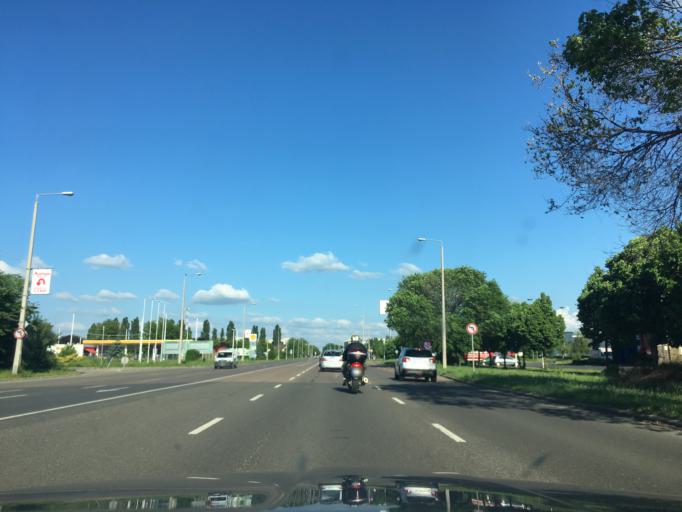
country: HU
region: Hajdu-Bihar
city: Debrecen
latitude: 47.5425
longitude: 21.5951
